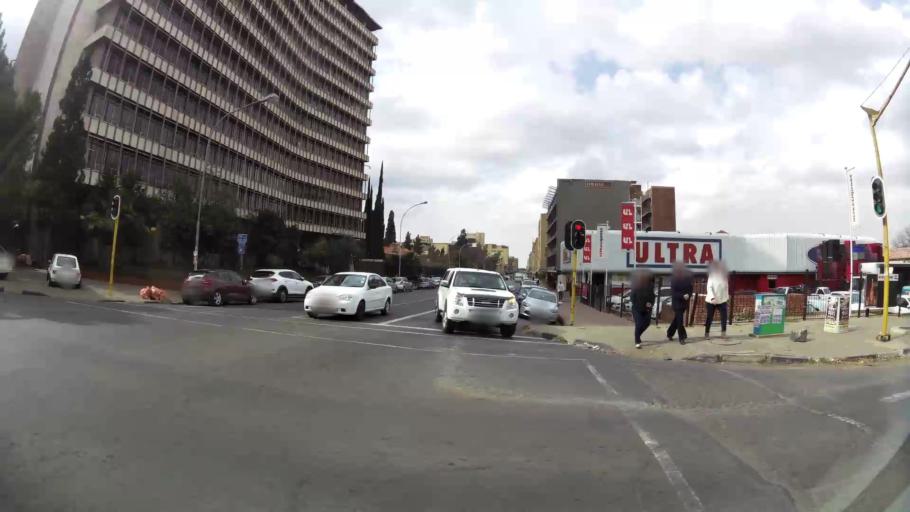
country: ZA
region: Orange Free State
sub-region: Mangaung Metropolitan Municipality
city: Bloemfontein
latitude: -29.1169
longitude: 26.2138
